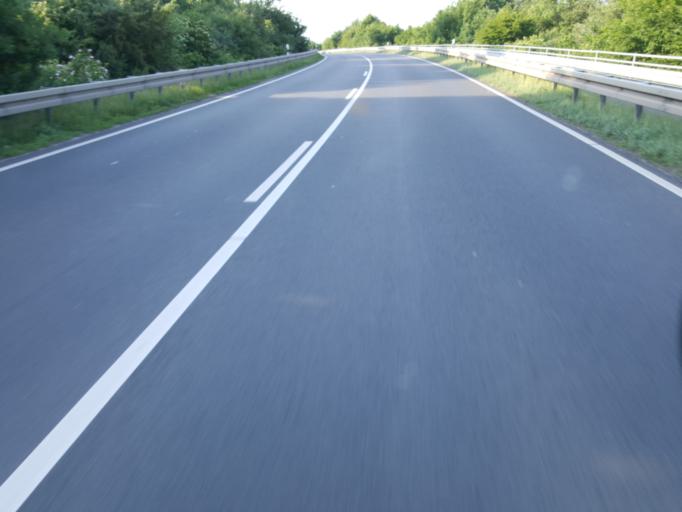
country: DE
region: Lower Saxony
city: Leese
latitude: 52.5228
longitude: 9.1229
